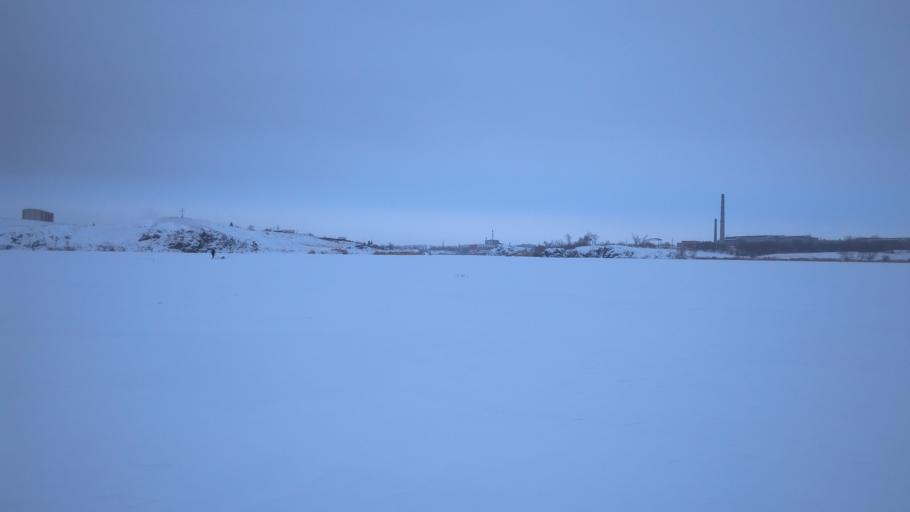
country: RU
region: Chelyabinsk
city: Troitsk
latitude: 54.0813
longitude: 61.5728
